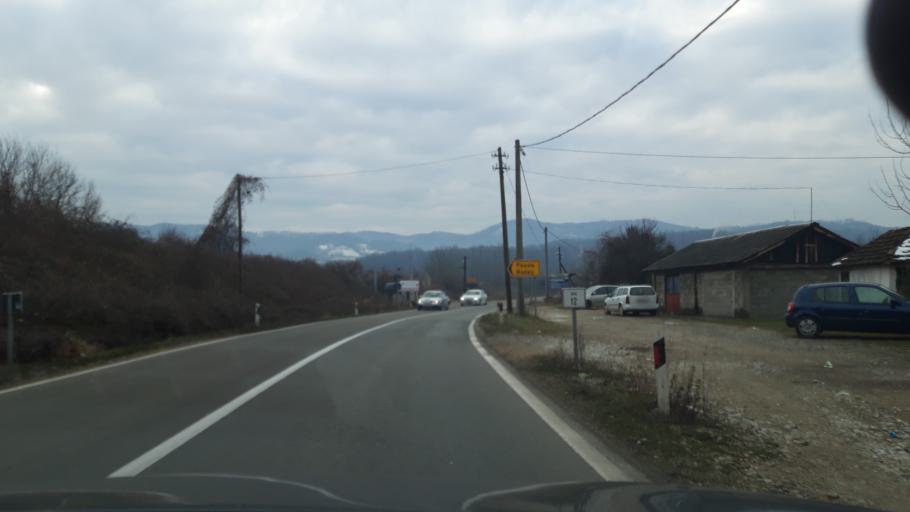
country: BA
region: Republika Srpska
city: Zvornik
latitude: 44.4128
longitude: 19.1487
